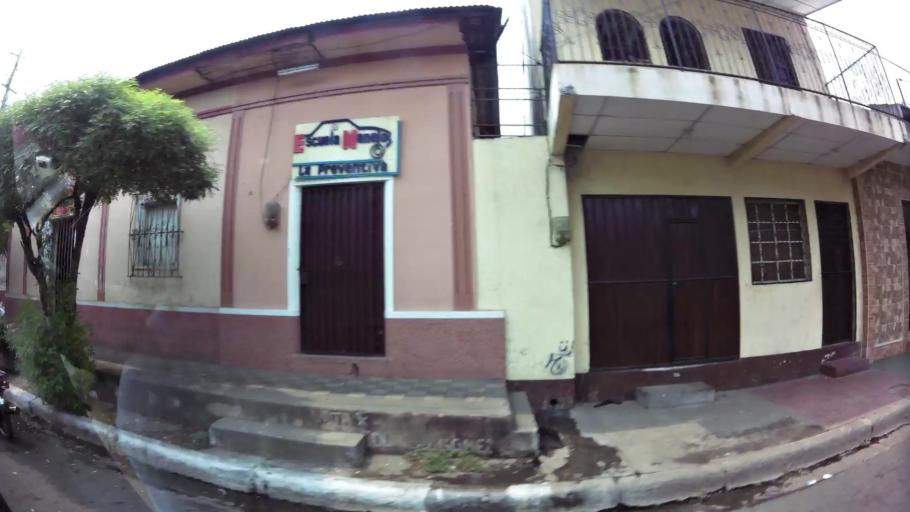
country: NI
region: Chinandega
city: Chinandega
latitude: 12.6336
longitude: -87.1330
